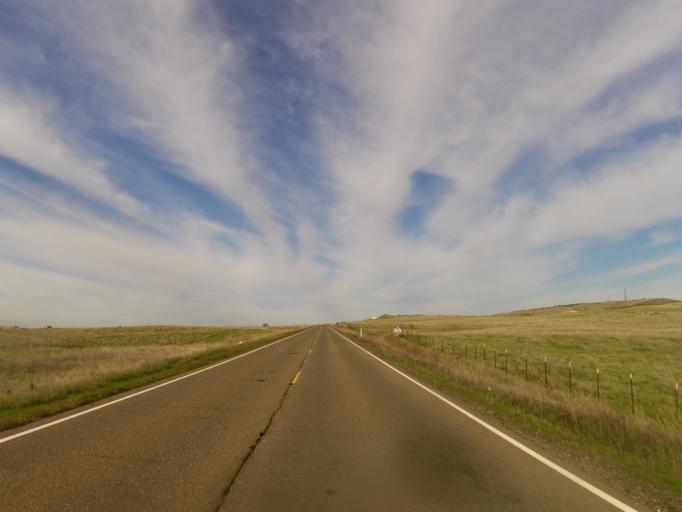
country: US
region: California
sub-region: El Dorado County
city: El Dorado Hills
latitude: 38.6307
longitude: -121.1141
